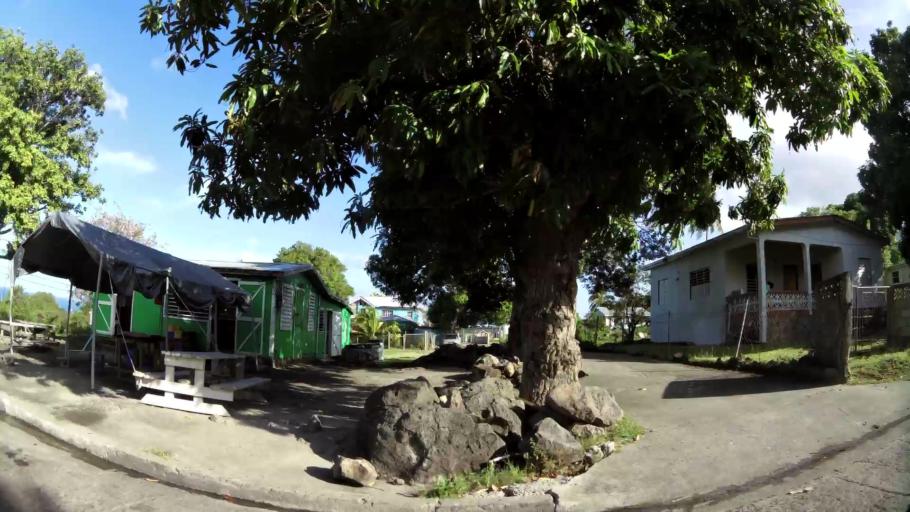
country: KN
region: Saint Paul Charlestown
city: Charlestown
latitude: 17.1433
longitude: -62.6216
